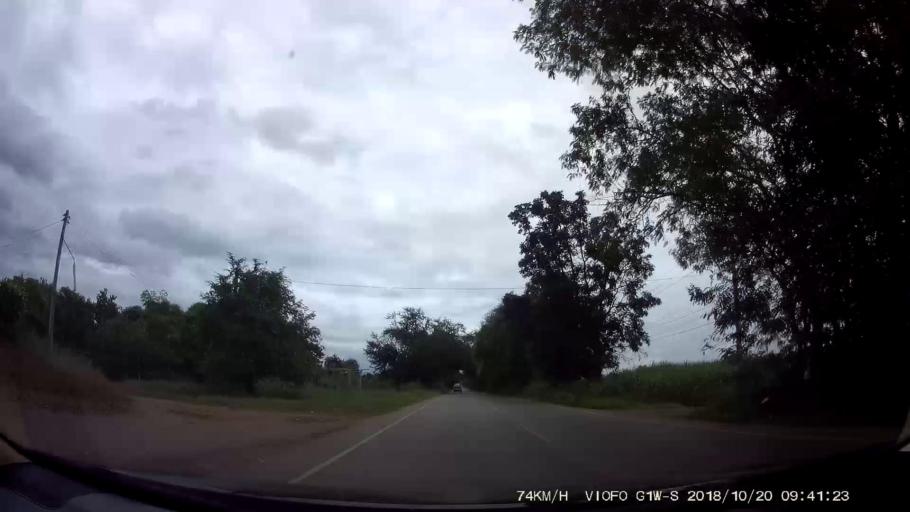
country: TH
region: Chaiyaphum
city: Khon San
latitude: 16.4528
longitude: 101.9572
